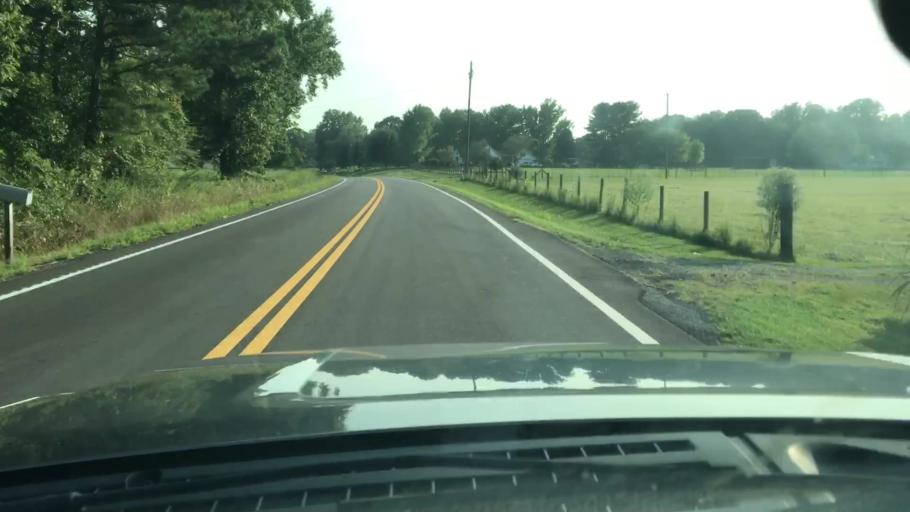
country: US
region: Tennessee
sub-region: Sumner County
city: Portland
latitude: 36.5647
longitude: -86.3856
